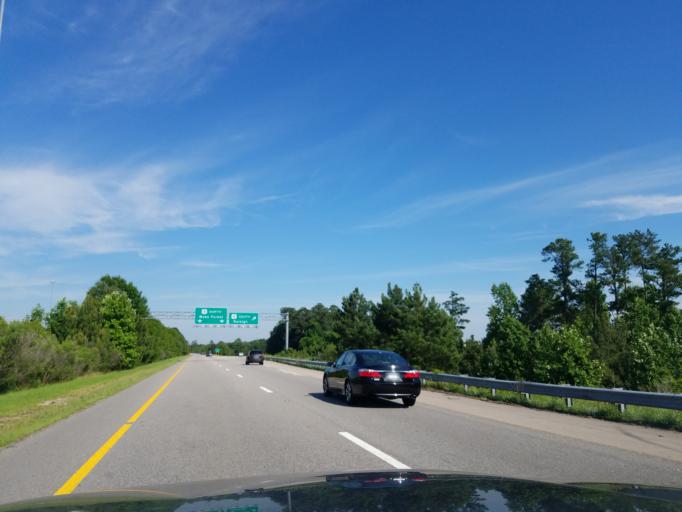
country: US
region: North Carolina
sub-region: Wake County
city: Raleigh
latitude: 35.8762
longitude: -78.5829
